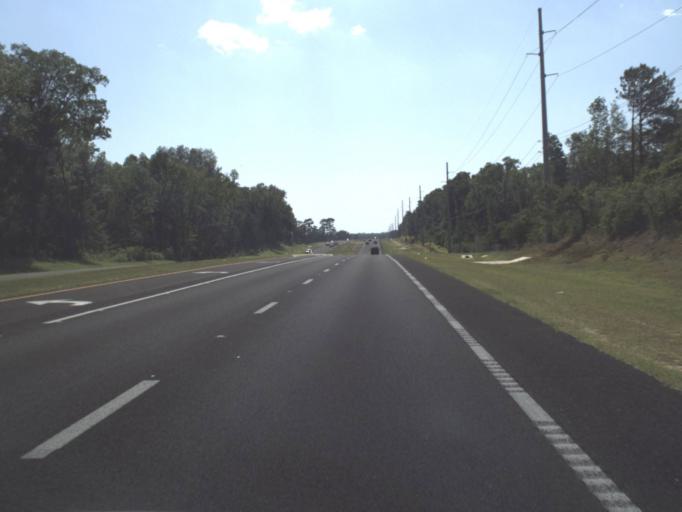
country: US
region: Florida
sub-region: Marion County
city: Ocala
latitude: 29.1870
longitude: -82.2753
